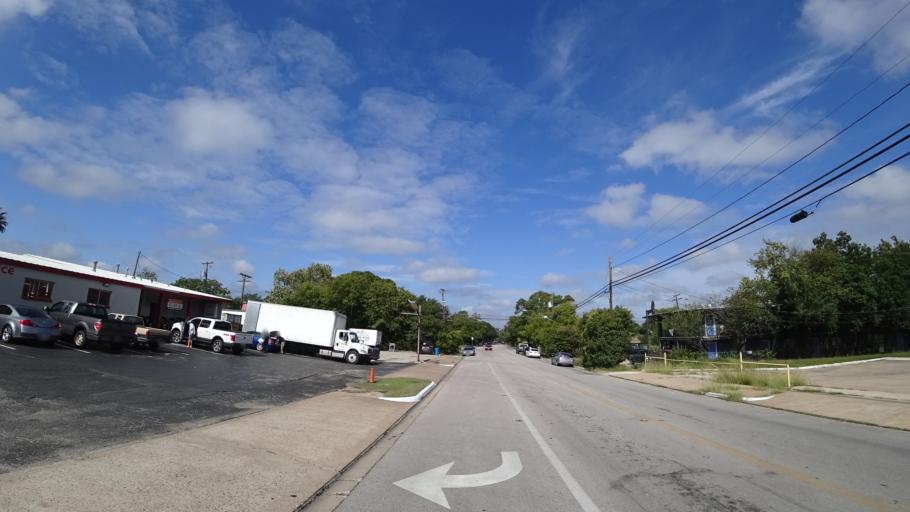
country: US
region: Texas
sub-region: Travis County
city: Austin
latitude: 30.3506
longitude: -97.7346
